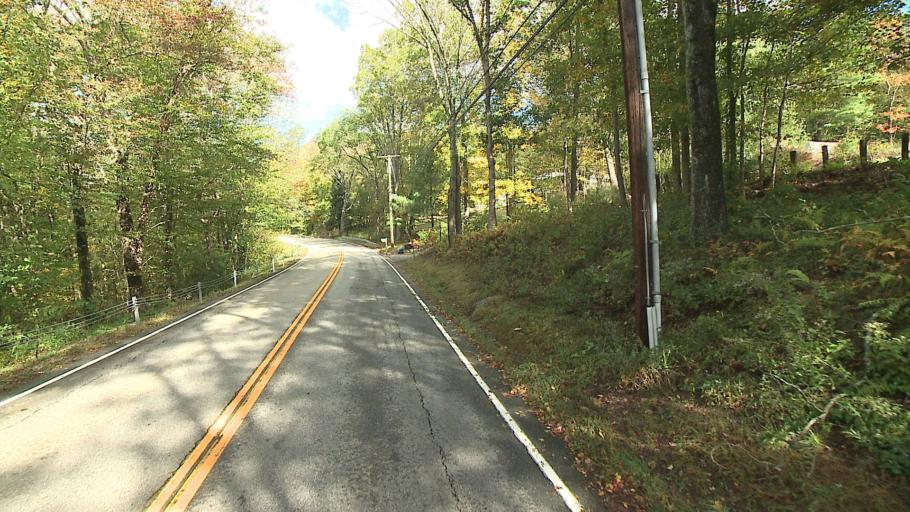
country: US
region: Connecticut
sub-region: Windham County
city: Putnam
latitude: 41.8871
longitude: -71.8759
